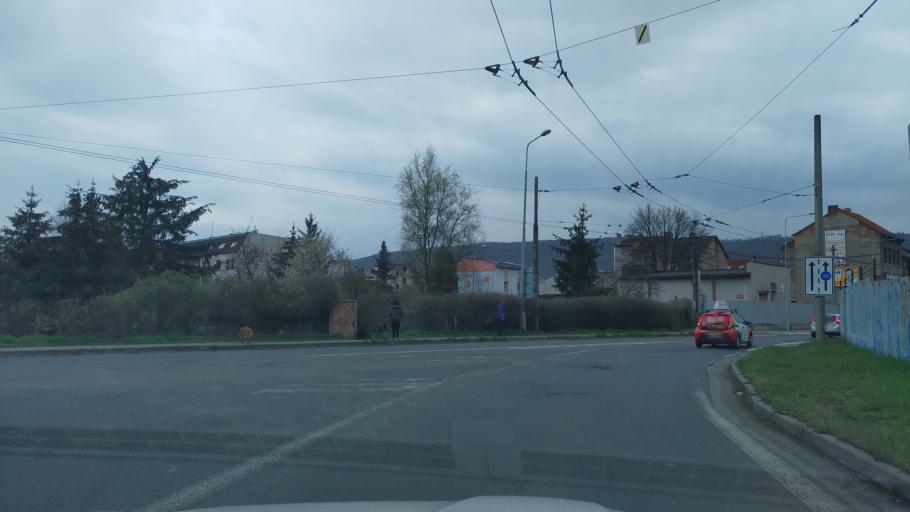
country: CZ
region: Ustecky
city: Trmice
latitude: 50.6540
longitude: 14.0011
